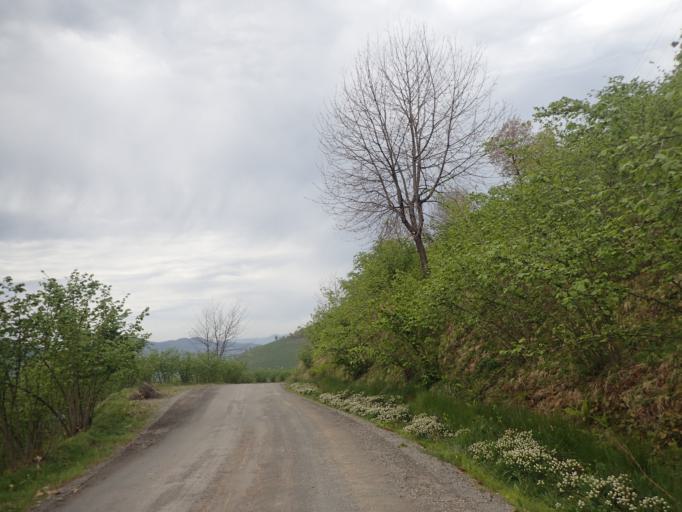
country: TR
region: Ordu
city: Kabaduz
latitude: 40.7944
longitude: 37.9036
